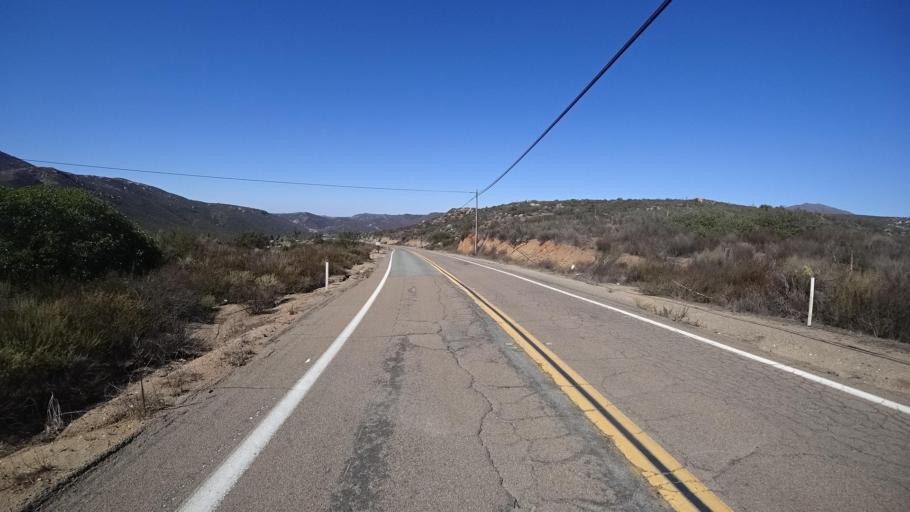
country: US
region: California
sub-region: San Diego County
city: Alpine
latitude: 32.7862
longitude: -116.7222
